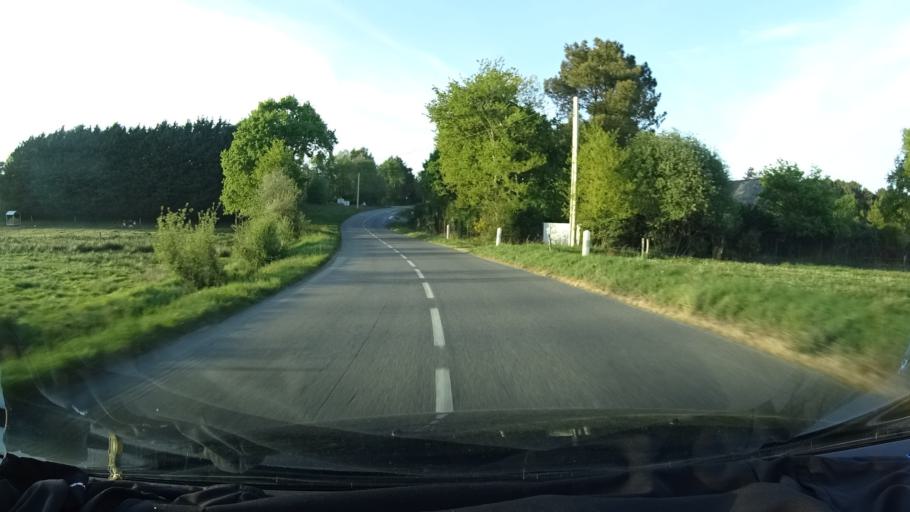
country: FR
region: Brittany
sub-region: Departement du Morbihan
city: Peaule
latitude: 47.5844
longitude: -2.3446
